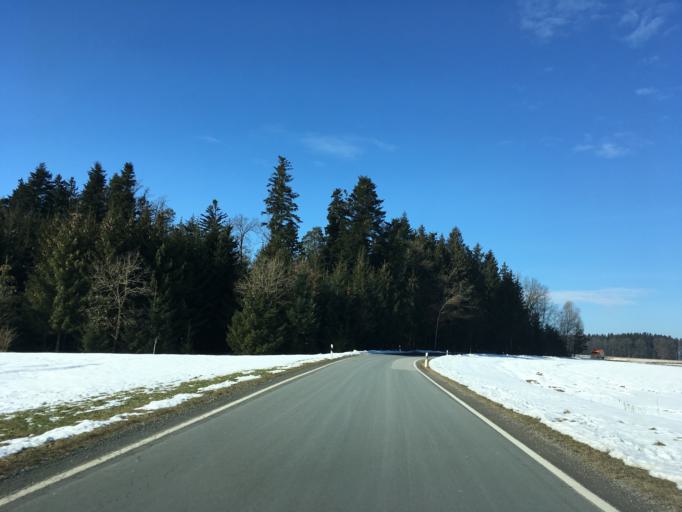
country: DE
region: Bavaria
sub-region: Upper Bavaria
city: Ramerberg
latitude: 48.0082
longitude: 12.1407
